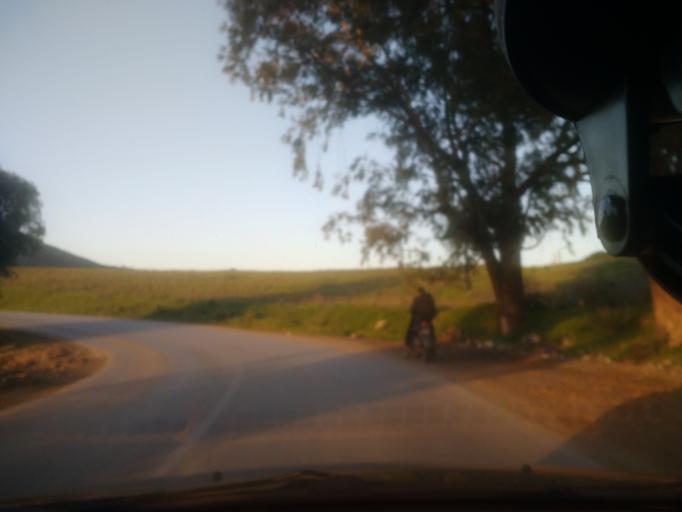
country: DZ
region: Boumerdes
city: Makouda
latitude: 36.7678
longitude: 4.0657
